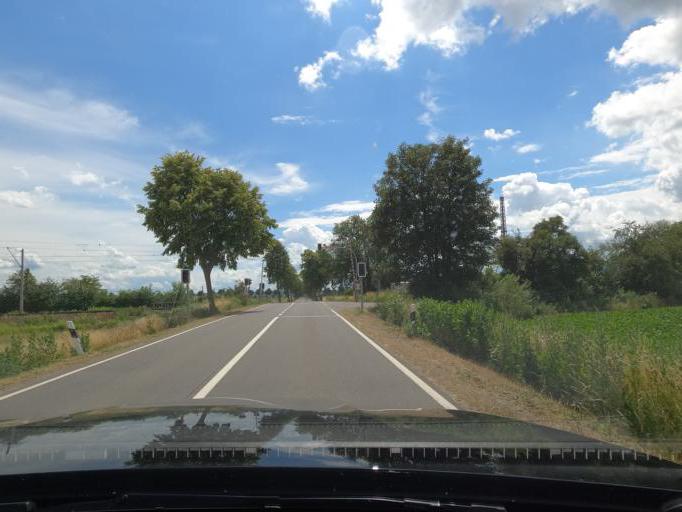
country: DE
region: Lower Saxony
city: Schellerten
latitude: 52.1795
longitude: 10.0414
